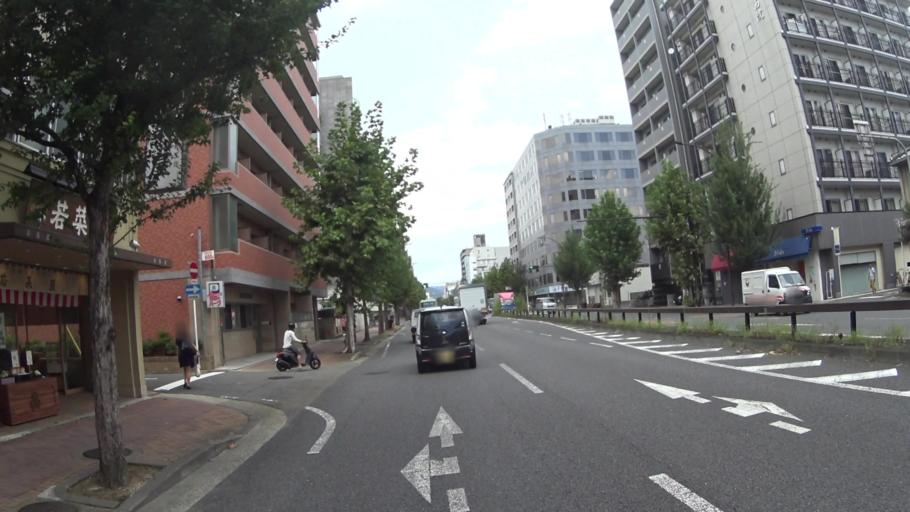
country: JP
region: Kyoto
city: Kyoto
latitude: 34.9991
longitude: 135.7320
